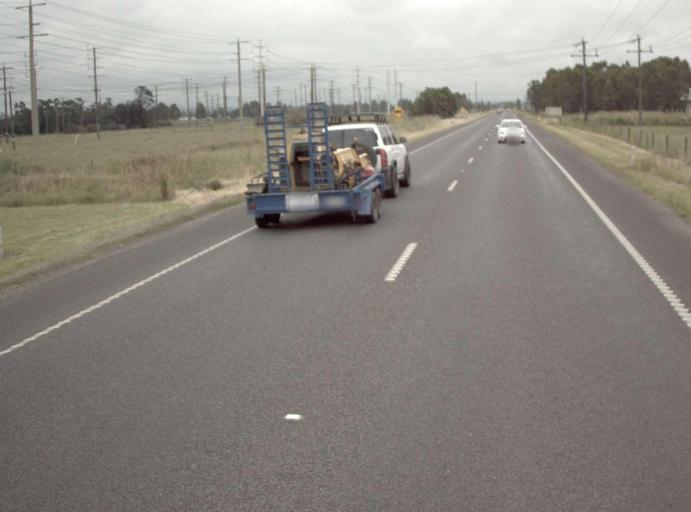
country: AU
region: Victoria
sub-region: Latrobe
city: Morwell
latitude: -38.2571
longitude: 146.4227
